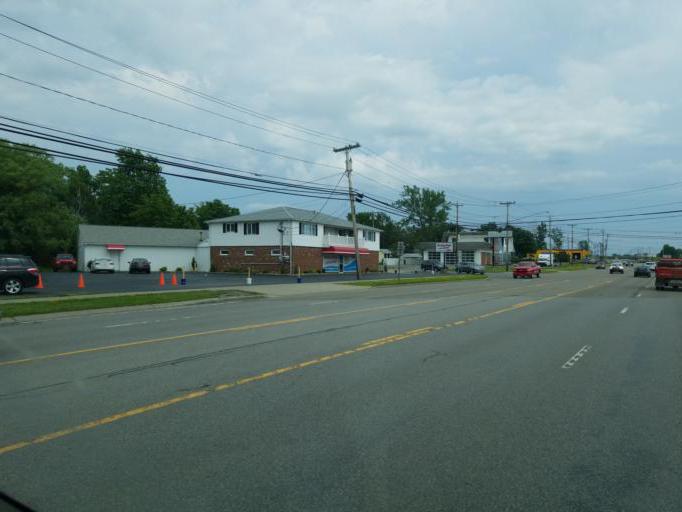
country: US
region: New York
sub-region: Erie County
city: Hamburg
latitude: 42.7478
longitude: -78.8532
